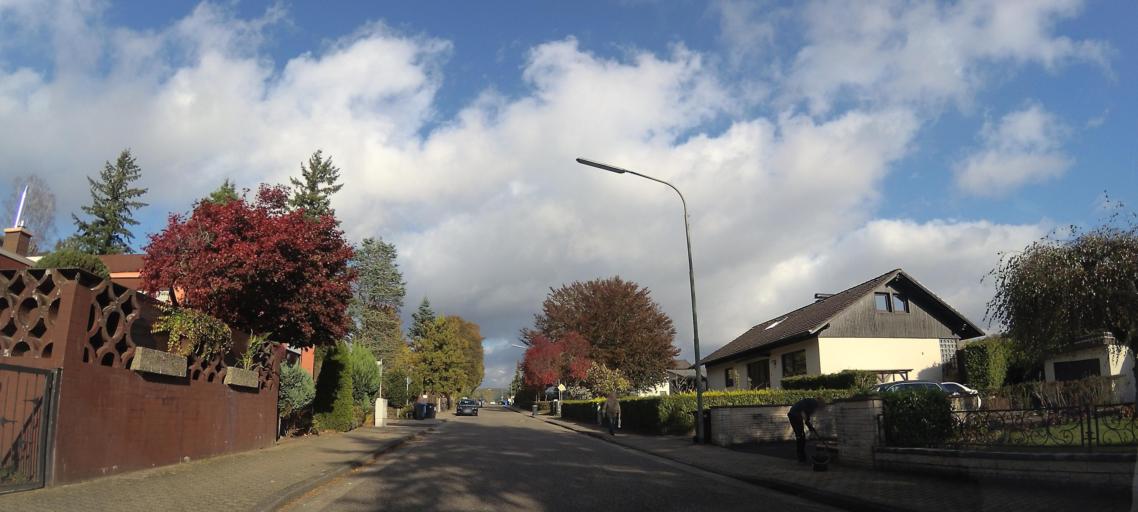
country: DE
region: Rheinland-Pfalz
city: Ruppertsweiler
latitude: 49.1932
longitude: 7.6763
